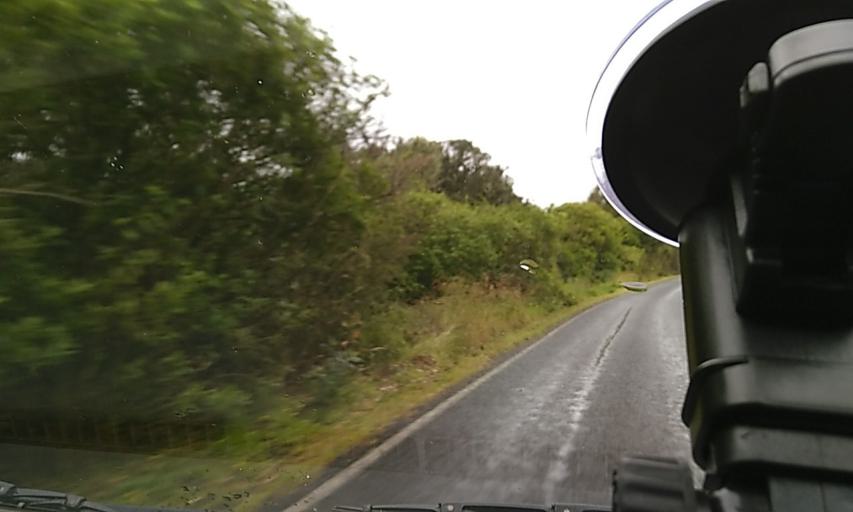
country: NZ
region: Auckland
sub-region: Auckland
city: Pukekohe East
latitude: -37.3178
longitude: 174.9368
